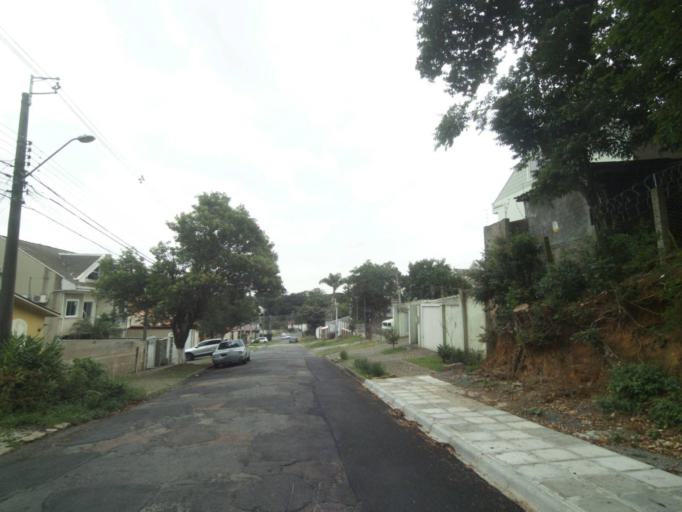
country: BR
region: Parana
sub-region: Curitiba
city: Curitiba
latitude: -25.4126
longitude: -49.3009
